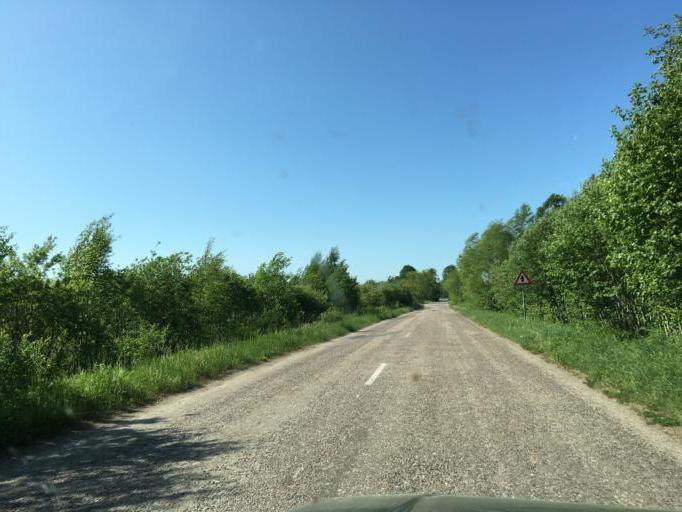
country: LV
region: Ventspils
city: Ventspils
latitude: 57.5024
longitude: 21.8453
